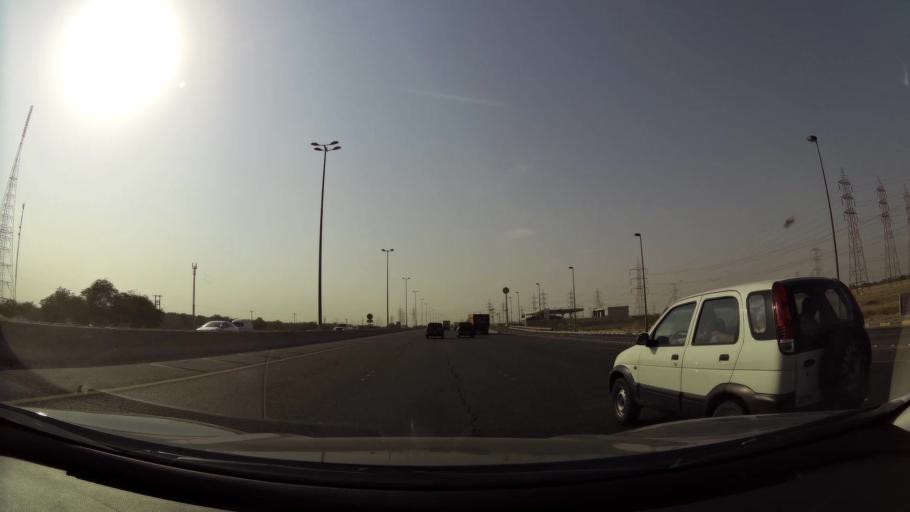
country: KW
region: Al Ahmadi
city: Al Ahmadi
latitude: 29.0820
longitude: 48.0995
